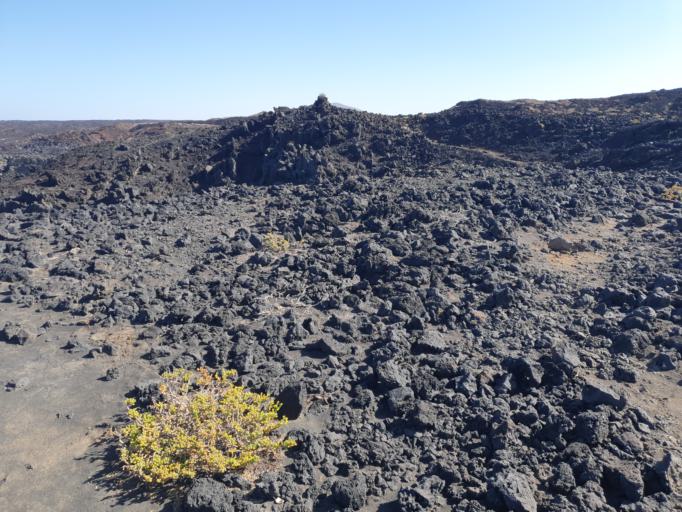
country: ES
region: Canary Islands
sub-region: Provincia de Las Palmas
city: Tinajo
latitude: 29.0651
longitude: -13.7649
